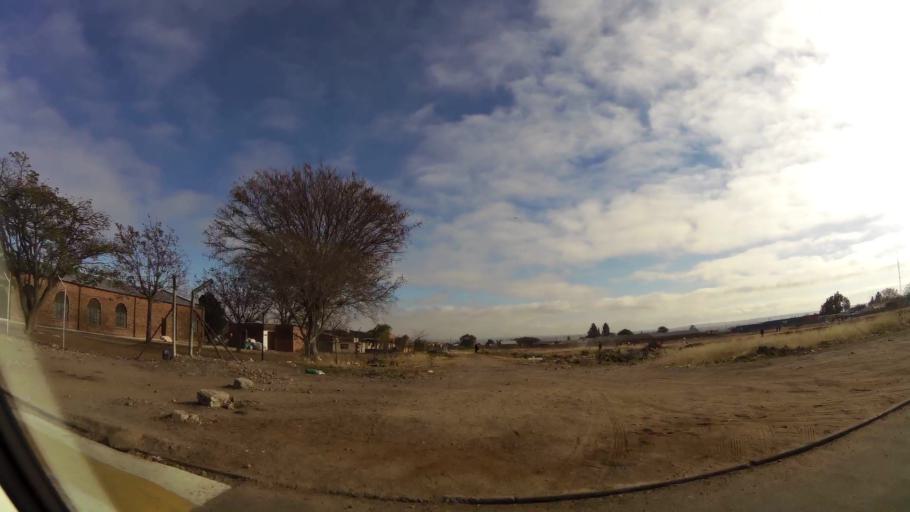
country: ZA
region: Limpopo
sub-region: Capricorn District Municipality
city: Polokwane
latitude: -23.8439
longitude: 29.3855
